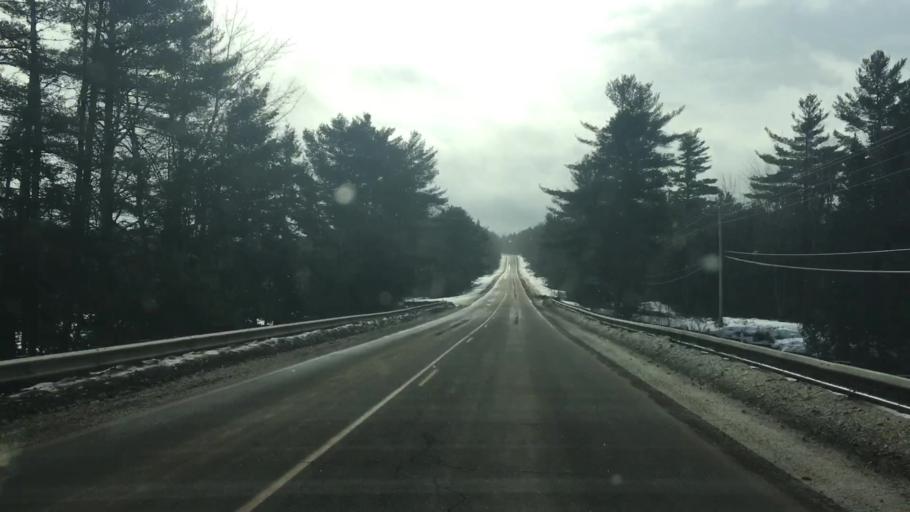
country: US
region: Maine
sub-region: Washington County
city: Calais
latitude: 45.0743
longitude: -67.3322
